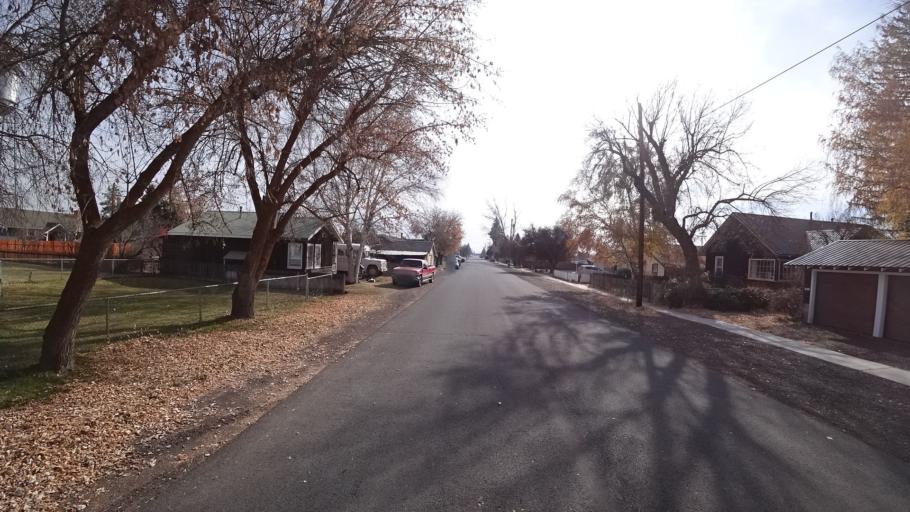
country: US
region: Oregon
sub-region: Klamath County
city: Klamath Falls
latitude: 41.9664
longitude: -121.9213
